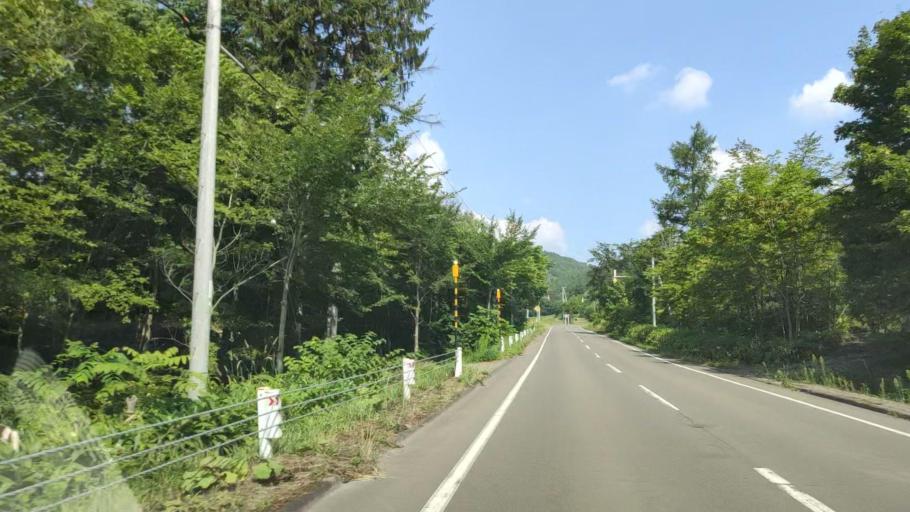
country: JP
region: Hokkaido
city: Shimo-furano
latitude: 43.4234
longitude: 142.4006
